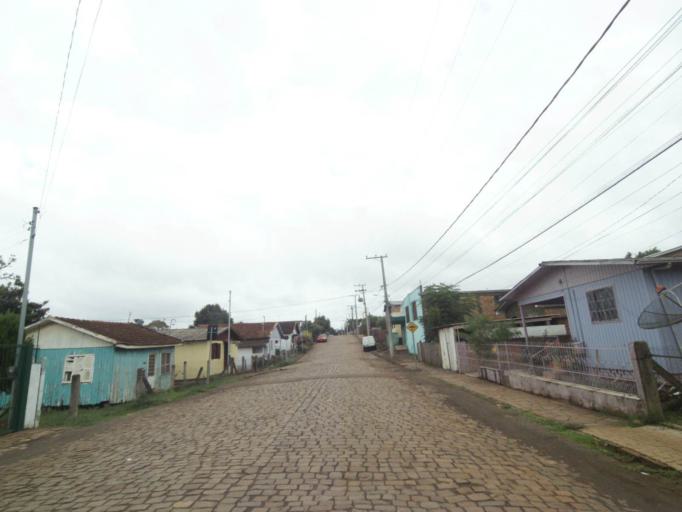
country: BR
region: Rio Grande do Sul
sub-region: Lagoa Vermelha
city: Lagoa Vermelha
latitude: -28.2227
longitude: -51.5205
